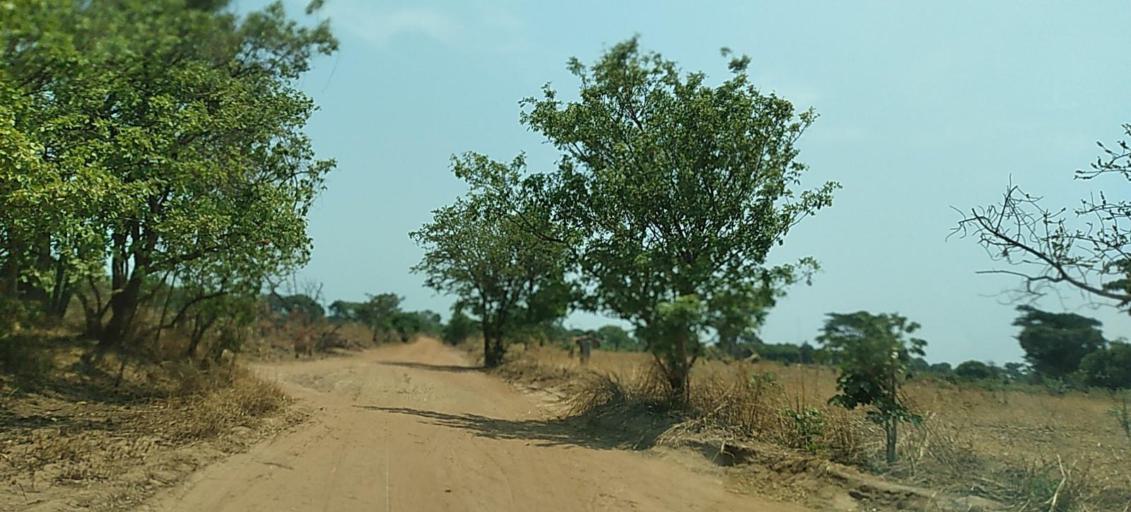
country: ZM
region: Copperbelt
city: Ndola
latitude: -13.0476
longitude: 28.7375
